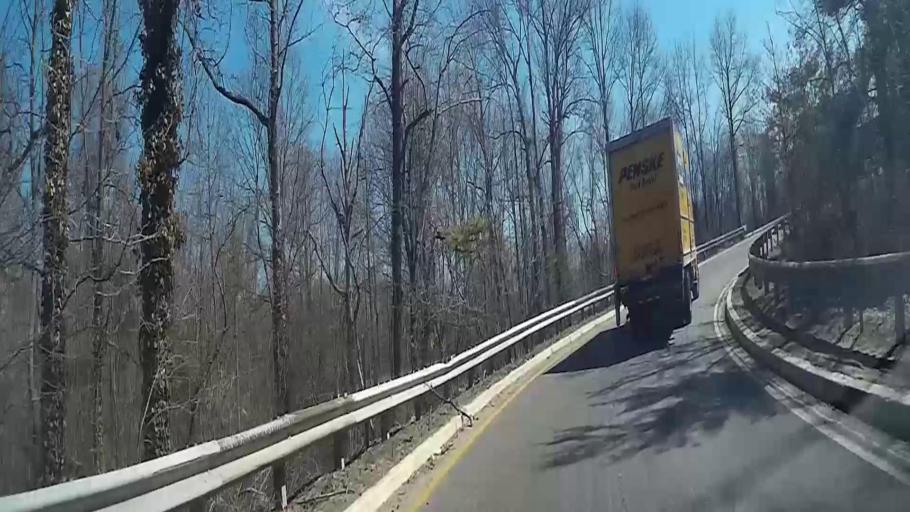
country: US
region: New Jersey
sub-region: Camden County
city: Kingston Estates
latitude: 39.9106
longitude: -74.9846
